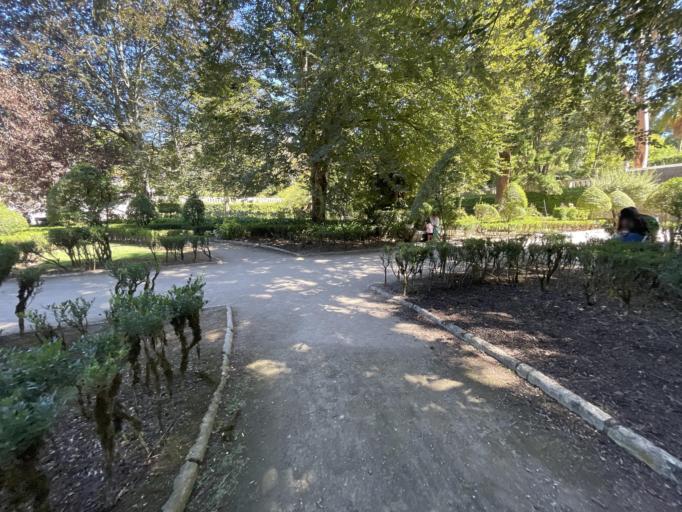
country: PT
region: Coimbra
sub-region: Coimbra
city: Coimbra
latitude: 40.2057
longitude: -8.4214
